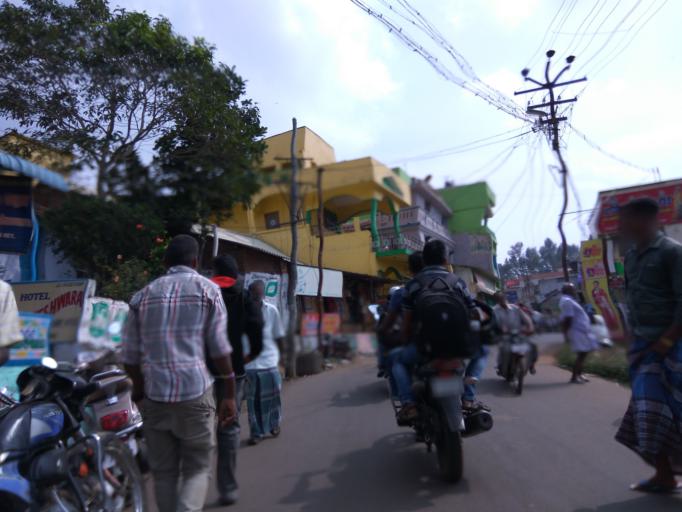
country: IN
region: Tamil Nadu
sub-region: Salem
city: Salem
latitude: 11.7753
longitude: 78.2095
